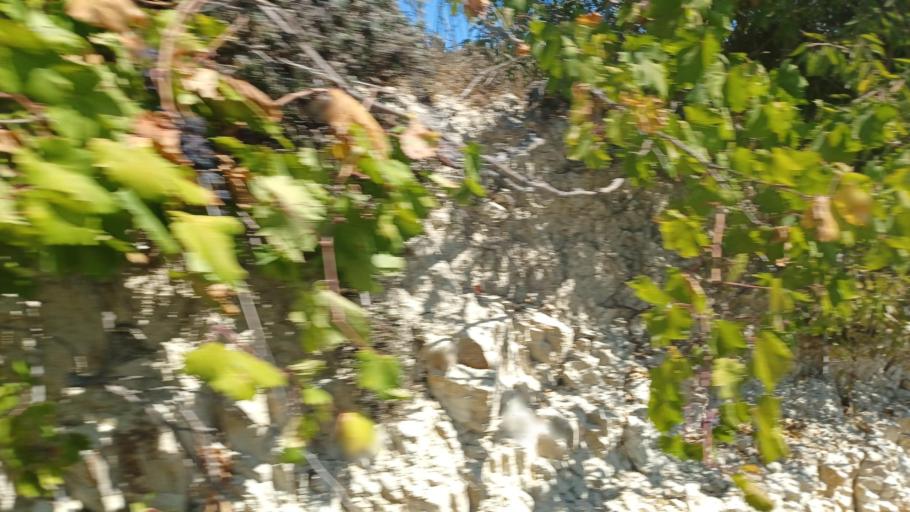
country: CY
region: Pafos
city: Mesogi
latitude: 34.8310
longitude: 32.4784
